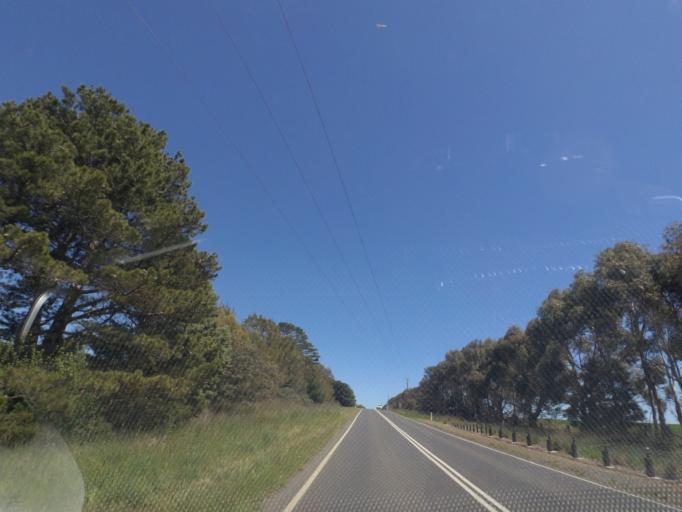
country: AU
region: Victoria
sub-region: Hume
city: Sunbury
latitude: -37.2850
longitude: 144.7735
